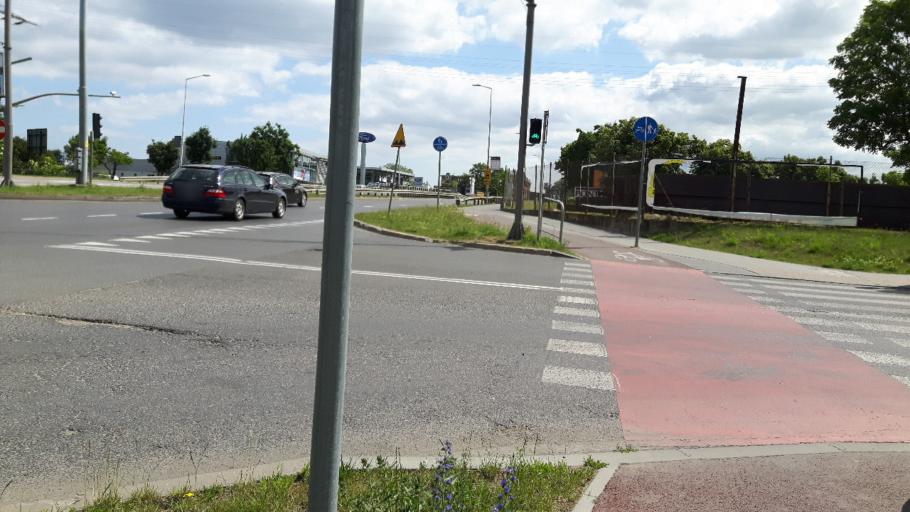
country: PL
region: Pomeranian Voivodeship
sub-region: Gdansk
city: Gdansk
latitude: 54.3492
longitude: 18.6754
